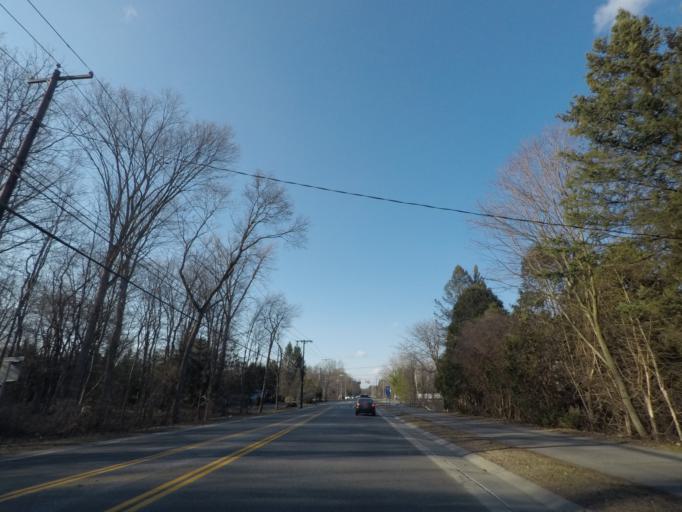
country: US
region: New York
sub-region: Saratoga County
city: Country Knolls
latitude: 42.8539
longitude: -73.7943
